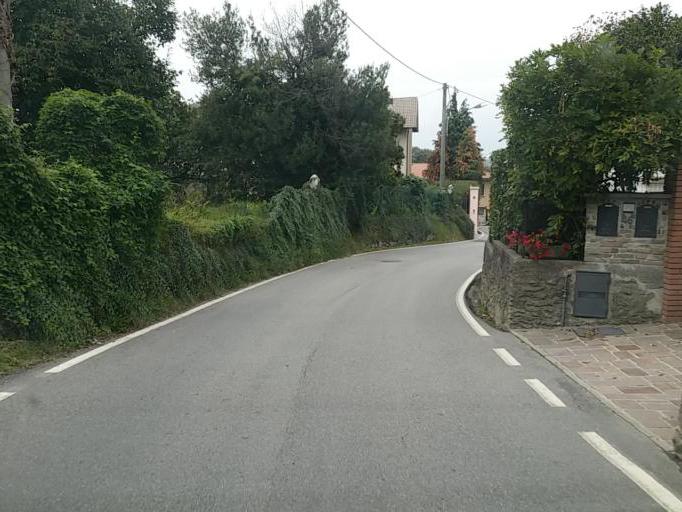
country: IT
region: Lombardy
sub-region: Provincia di Varese
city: Inarzo
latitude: 45.7785
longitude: 8.7319
